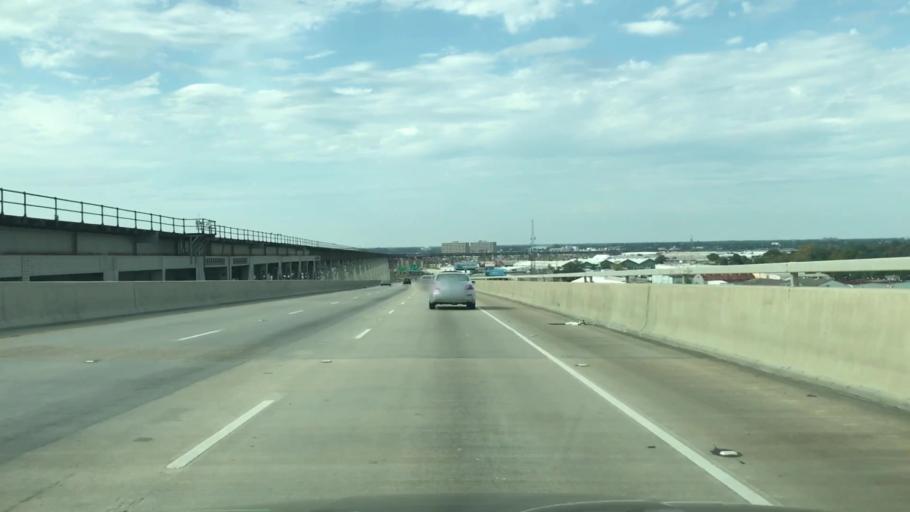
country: US
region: Louisiana
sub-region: Jefferson Parish
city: Bridge City
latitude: 29.9473
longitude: -90.1722
